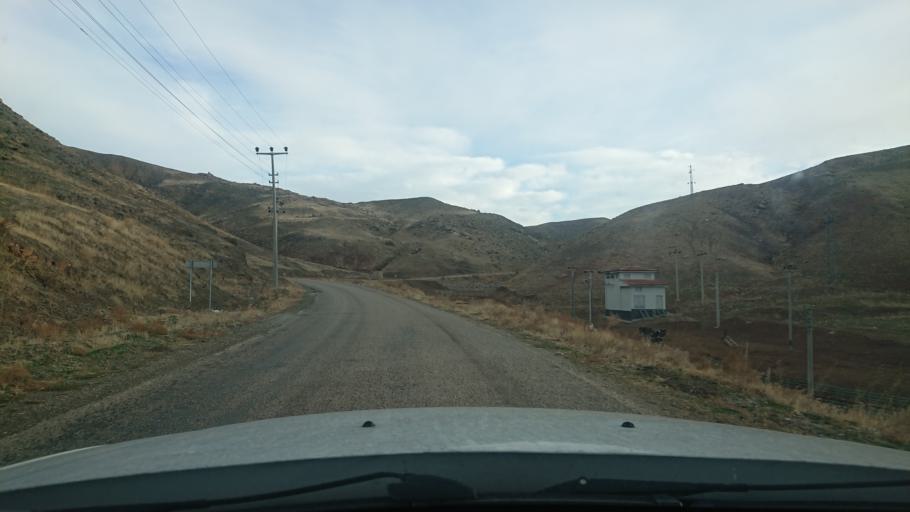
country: TR
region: Aksaray
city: Acipinar
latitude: 38.6200
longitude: 33.7877
